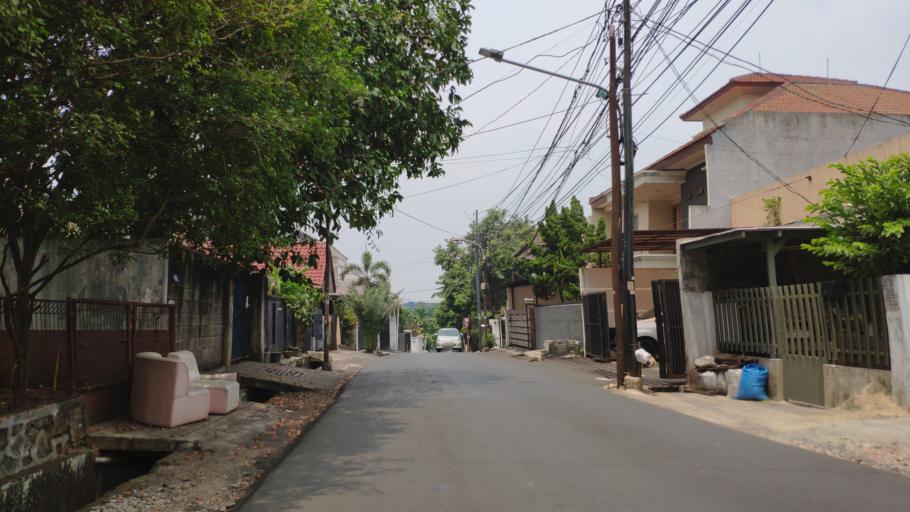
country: ID
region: Banten
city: South Tangerang
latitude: -6.2665
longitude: 106.7725
